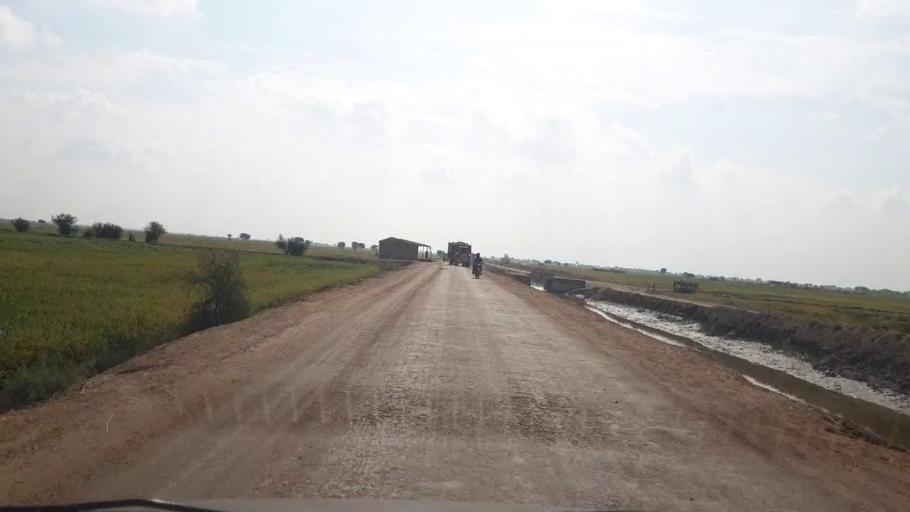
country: PK
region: Sindh
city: Kario
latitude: 24.5832
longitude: 68.5773
